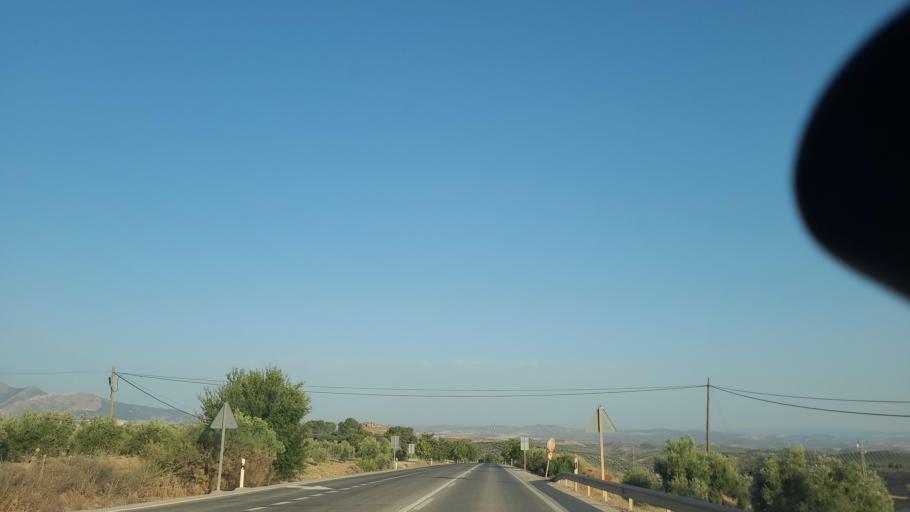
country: ES
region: Andalusia
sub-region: Provincia de Jaen
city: Mancha Real
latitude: 37.8034
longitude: -3.6446
